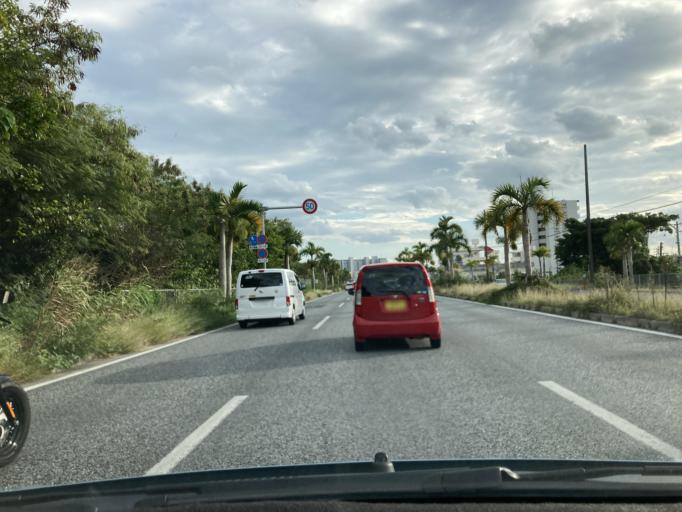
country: JP
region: Okinawa
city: Chatan
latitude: 26.3349
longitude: 127.7516
